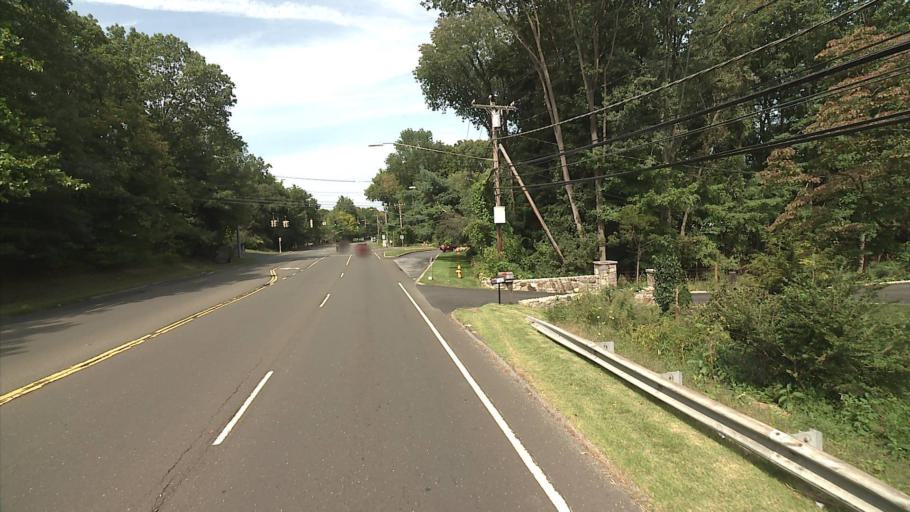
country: US
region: Connecticut
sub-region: Fairfield County
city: North Stamford
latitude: 41.0949
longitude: -73.5631
